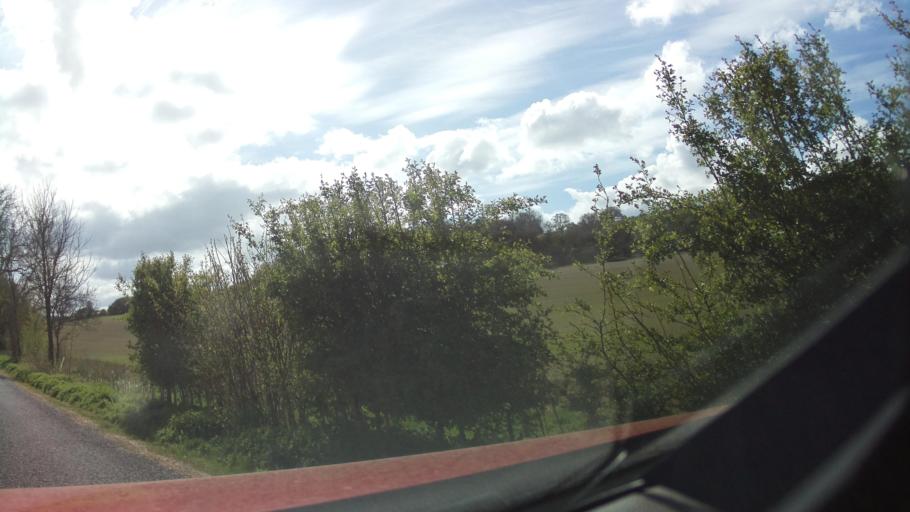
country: GB
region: England
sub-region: West Berkshire
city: Kintbury
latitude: 51.3362
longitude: -1.4699
